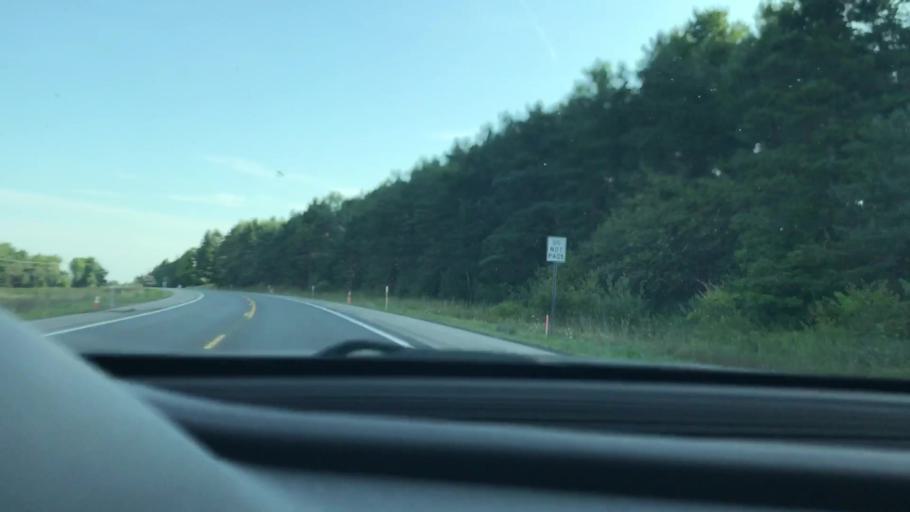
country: US
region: Michigan
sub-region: Antrim County
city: Bellaire
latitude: 45.0387
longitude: -85.3496
